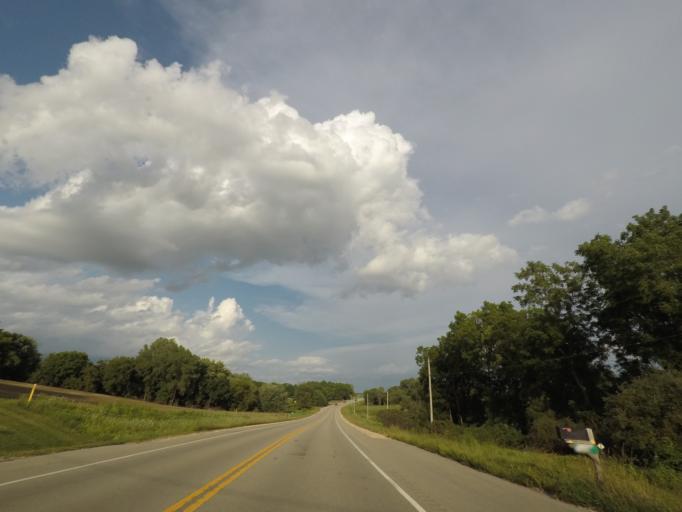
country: US
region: Wisconsin
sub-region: Dane County
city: Waunakee
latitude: 43.1910
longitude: -89.5357
